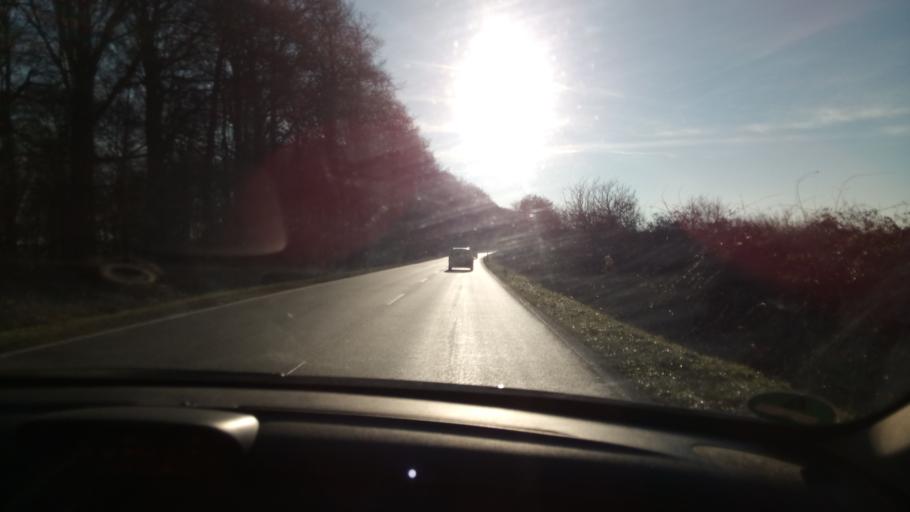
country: DE
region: Schleswig-Holstein
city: Buchhorst
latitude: 53.4012
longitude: 10.5587
